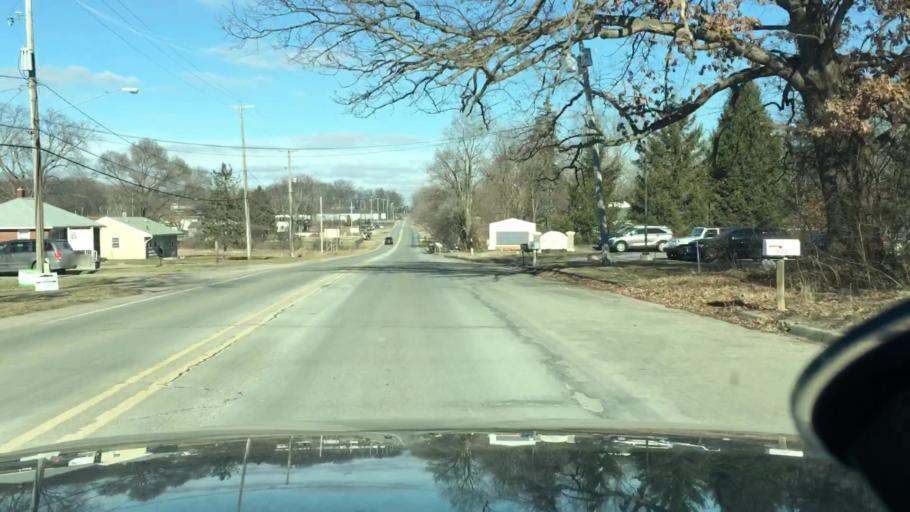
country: US
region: Michigan
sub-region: Jackson County
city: Jackson
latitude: 42.2806
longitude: -84.4300
